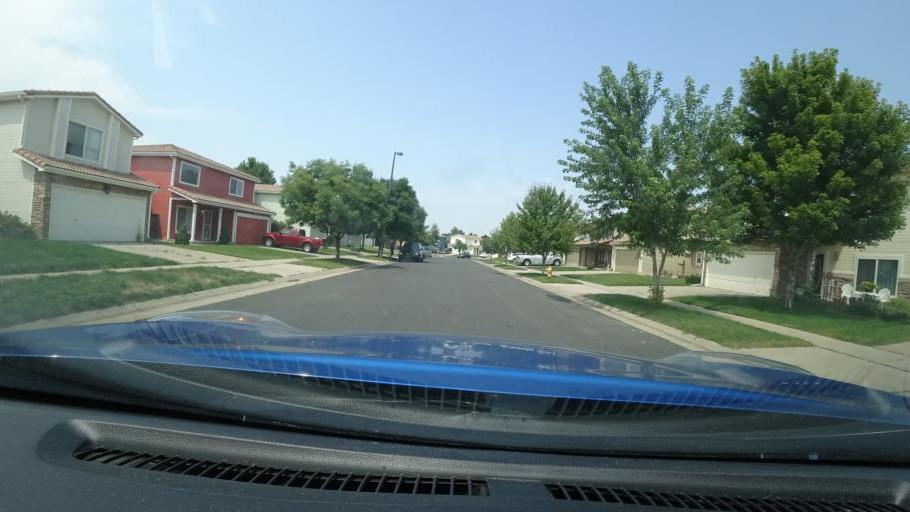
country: US
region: Colorado
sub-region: Adams County
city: Aurora
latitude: 39.7732
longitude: -104.7408
